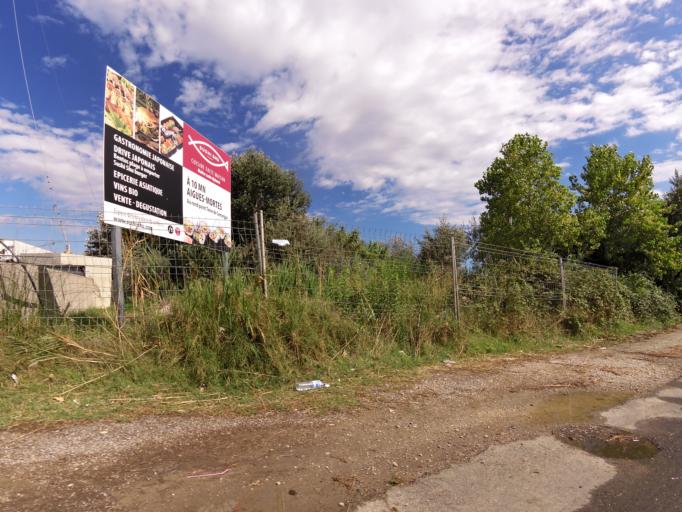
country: FR
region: Languedoc-Roussillon
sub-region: Departement du Gard
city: Le Grau-du-Roi
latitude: 43.5222
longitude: 4.1497
